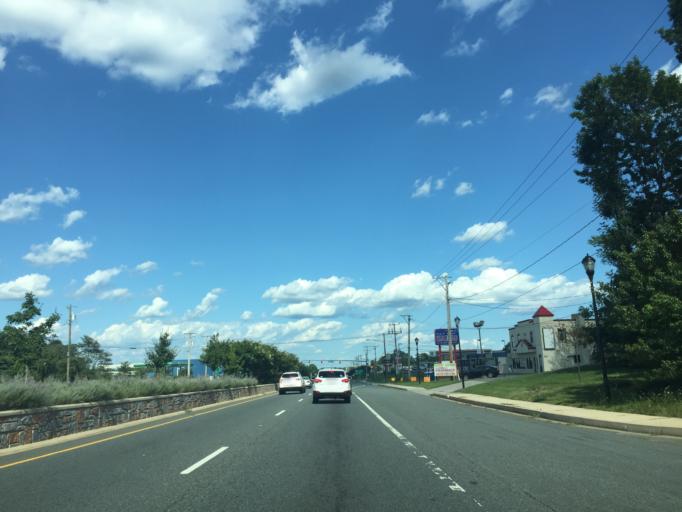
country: US
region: Maryland
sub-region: Harford County
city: Edgewood
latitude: 39.4341
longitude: -76.3222
